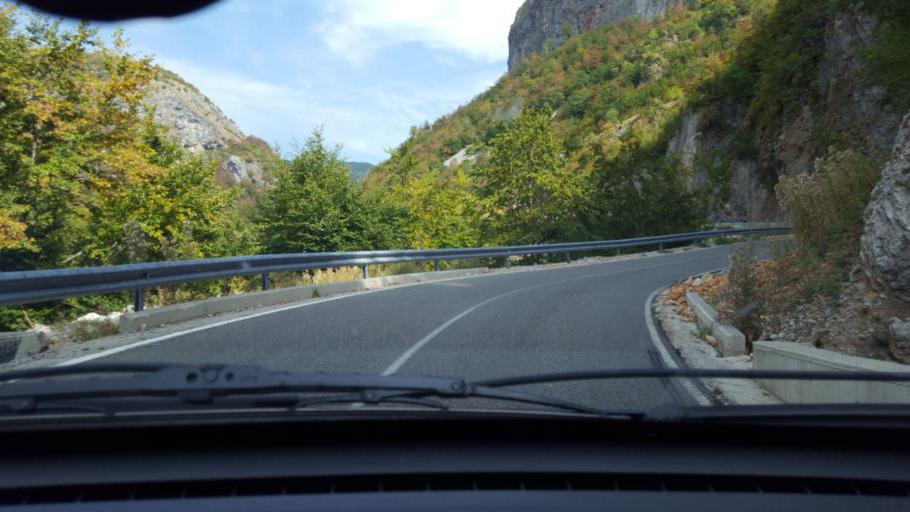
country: ME
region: Andrijevica
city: Andrijevica
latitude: 42.5329
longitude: 19.6689
